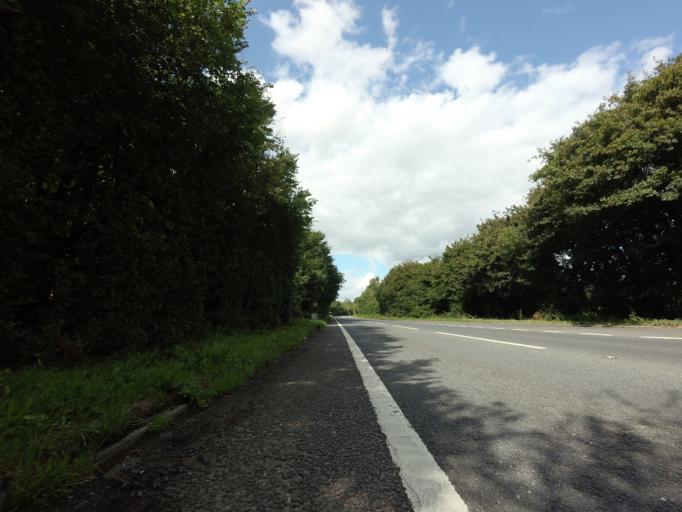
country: GB
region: England
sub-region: Kent
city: Borough Green
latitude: 51.2879
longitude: 0.2832
